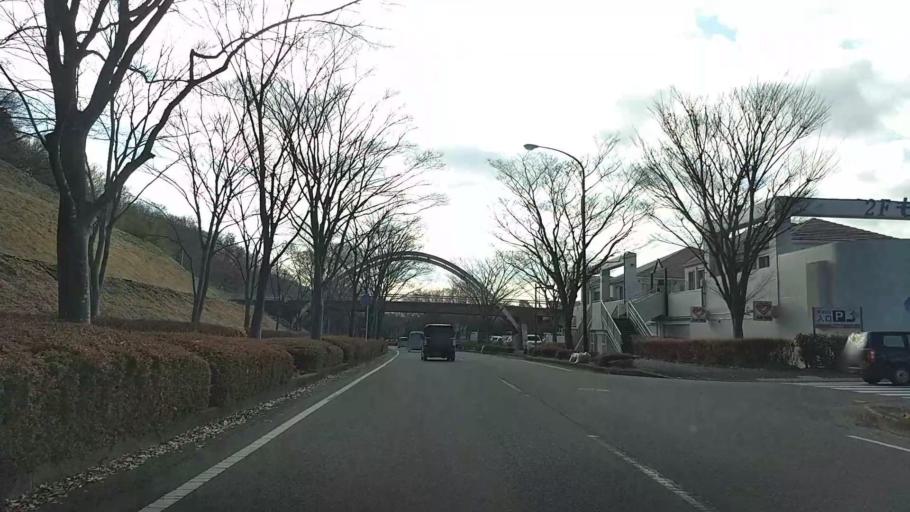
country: JP
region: Kanagawa
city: Atsugi
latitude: 35.4459
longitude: 139.3110
